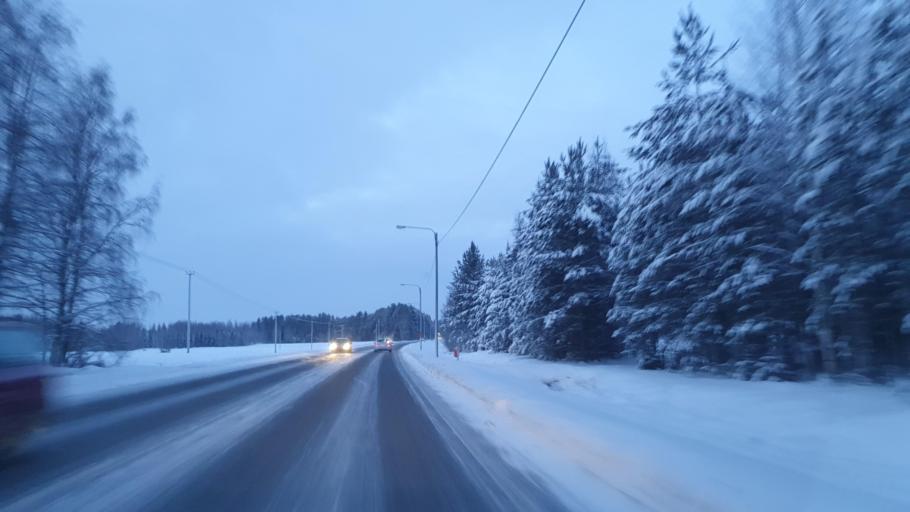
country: FI
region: Northern Ostrobothnia
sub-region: Oulu
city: Muhos
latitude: 64.8710
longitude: 25.8643
